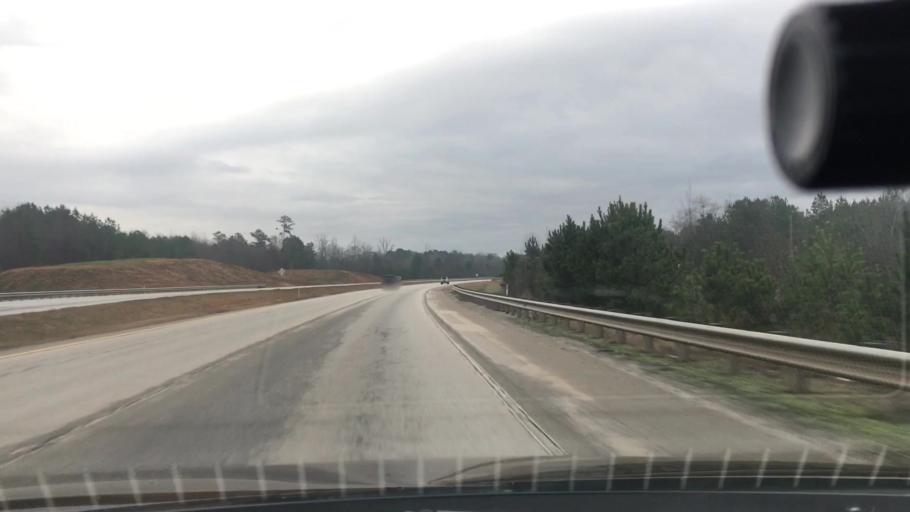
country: US
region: Georgia
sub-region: Henry County
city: Locust Grove
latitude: 33.2603
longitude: -84.1263
